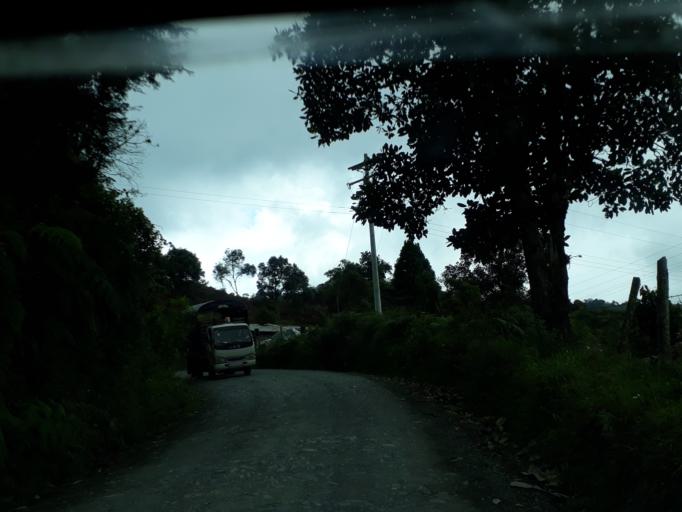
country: CO
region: Cundinamarca
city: Pacho
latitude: 5.2460
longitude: -74.1839
